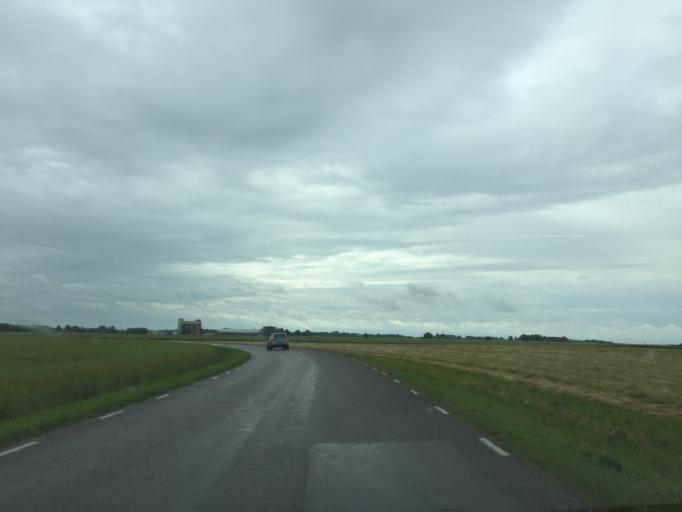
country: SE
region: OEstergoetland
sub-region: Vadstena Kommun
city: Vadstena
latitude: 58.4415
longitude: 14.8445
